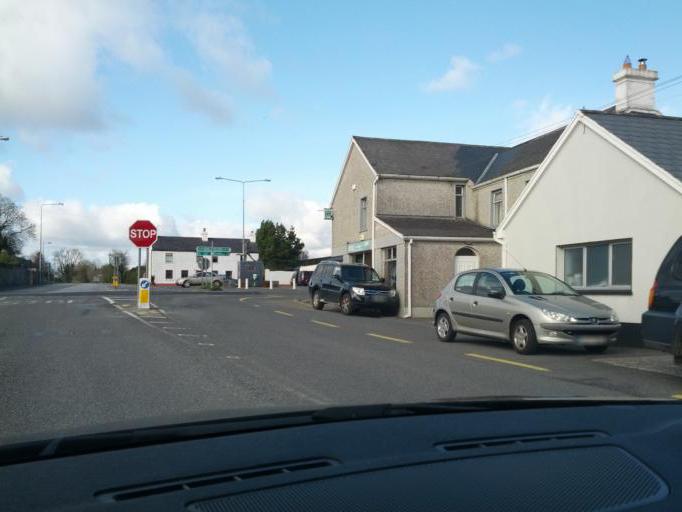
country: IE
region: Connaught
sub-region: County Galway
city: Athenry
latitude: 53.4876
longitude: -8.5682
